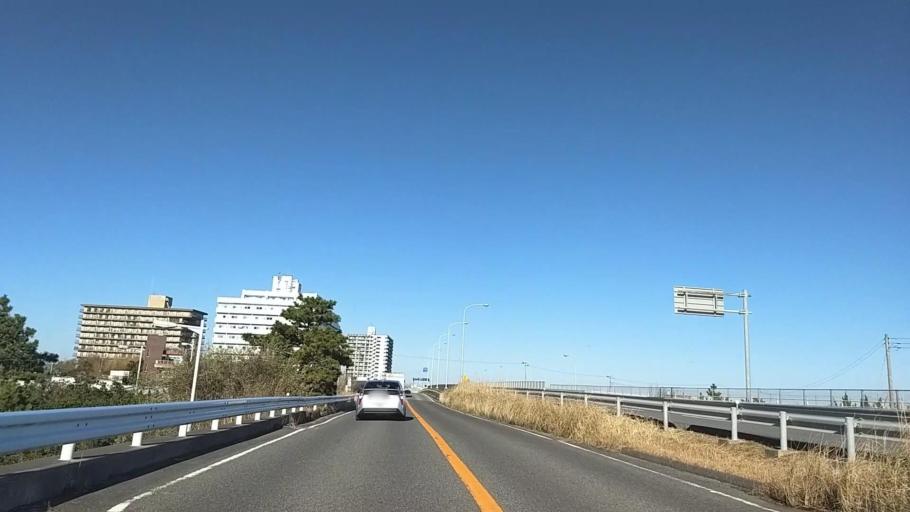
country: JP
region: Chiba
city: Mobara
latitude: 35.4485
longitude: 140.4020
